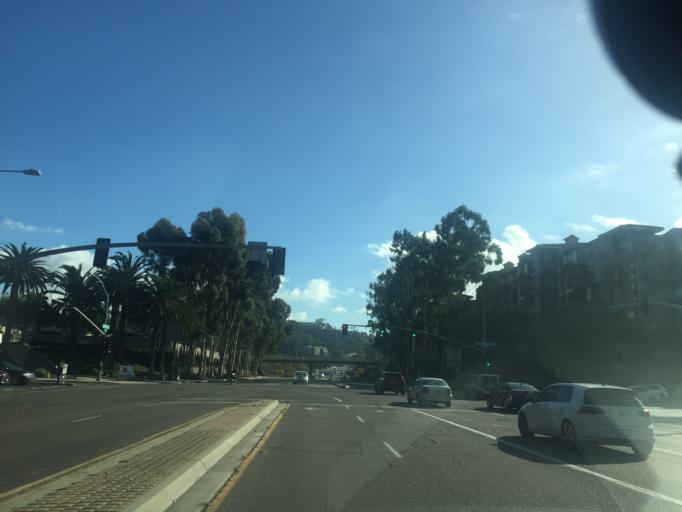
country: US
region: California
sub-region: San Diego County
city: San Diego
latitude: 32.7761
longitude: -117.1413
